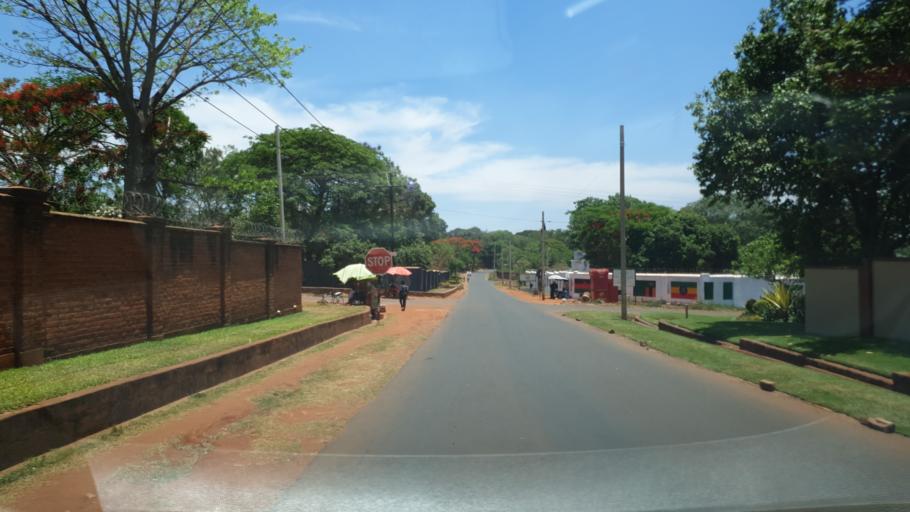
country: MW
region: Central Region
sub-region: Lilongwe District
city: Lilongwe
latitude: -13.9831
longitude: 33.7524
